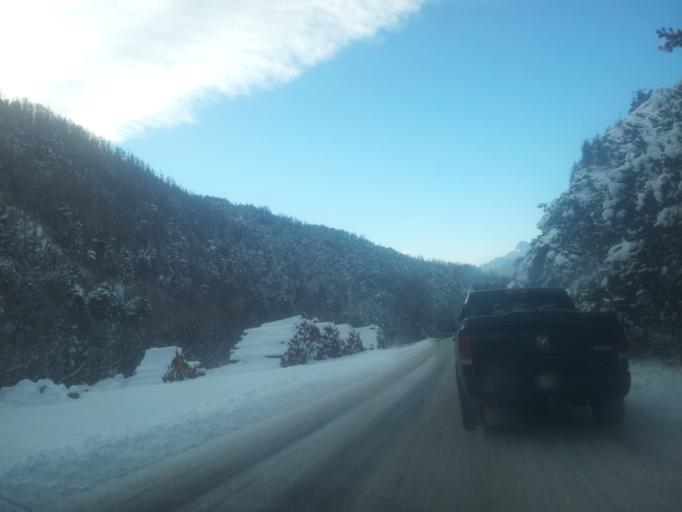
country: FR
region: Provence-Alpes-Cote d'Azur
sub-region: Departement des Hautes-Alpes
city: Embrun
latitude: 44.5573
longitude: 6.5625
